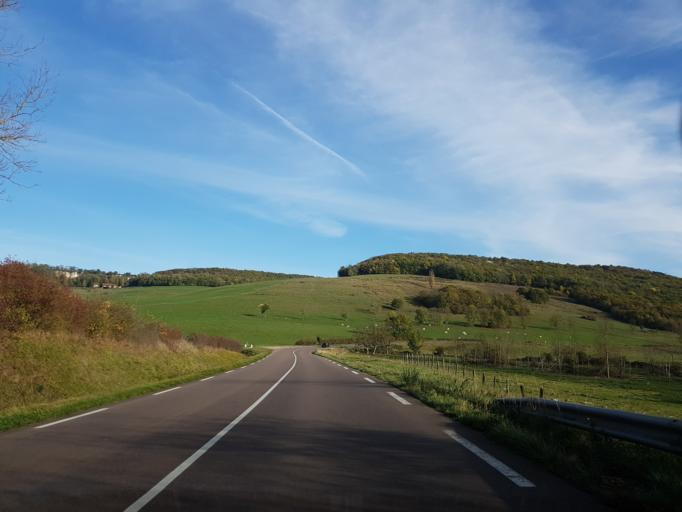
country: FR
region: Bourgogne
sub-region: Departement de la Cote-d'Or
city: Vitteaux
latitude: 47.3820
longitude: 4.5563
